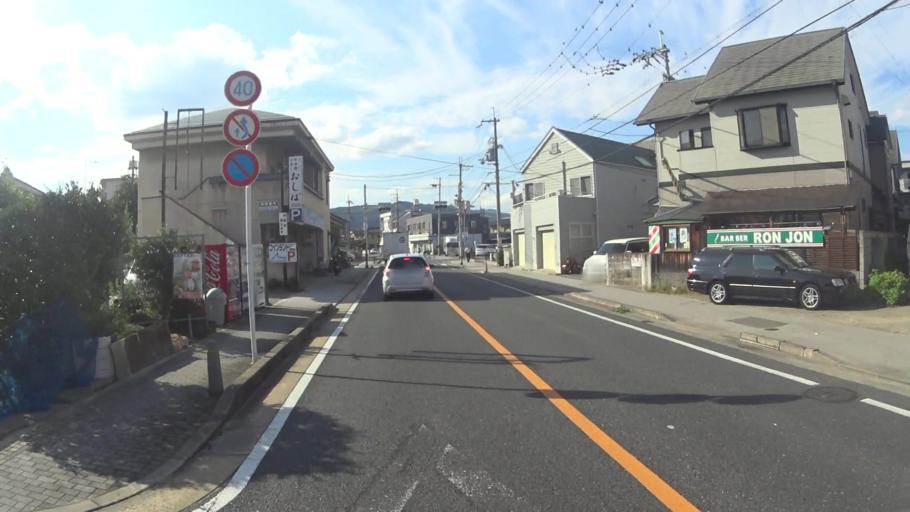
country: JP
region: Kyoto
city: Yawata
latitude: 34.8839
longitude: 135.7054
